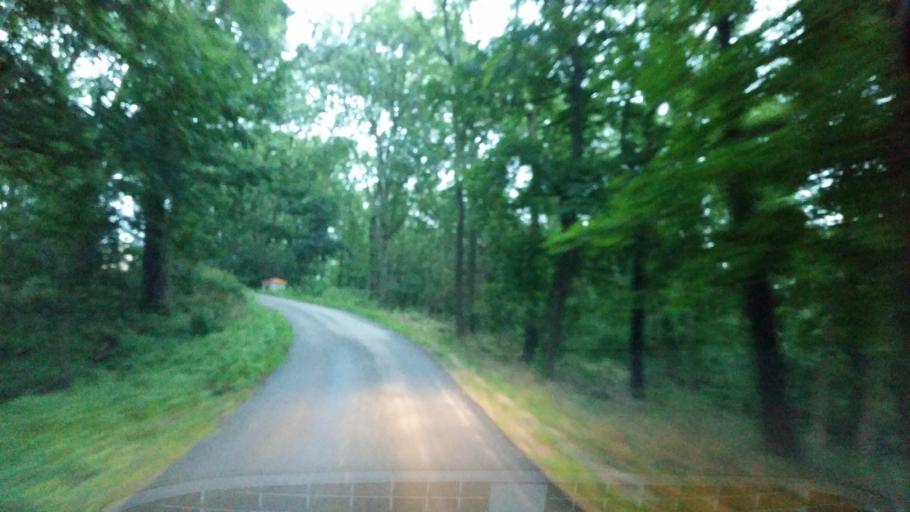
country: DE
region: Saxony
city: Sohland am Rotstein
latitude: 51.1089
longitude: 14.7636
